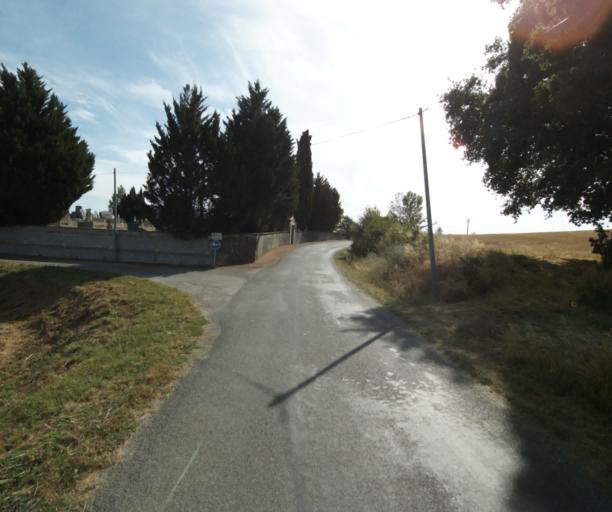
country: FR
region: Midi-Pyrenees
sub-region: Departement du Tarn
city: Puylaurens
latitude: 43.5250
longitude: 2.0562
